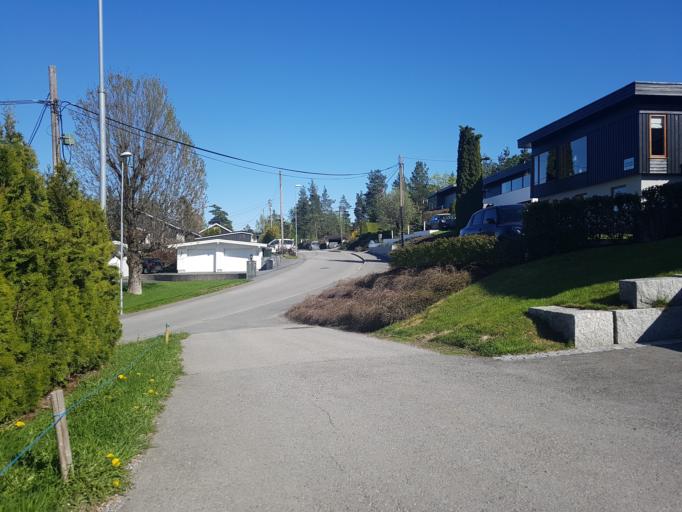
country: NO
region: Buskerud
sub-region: Drammen
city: Drammen
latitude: 59.7238
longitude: 10.2086
